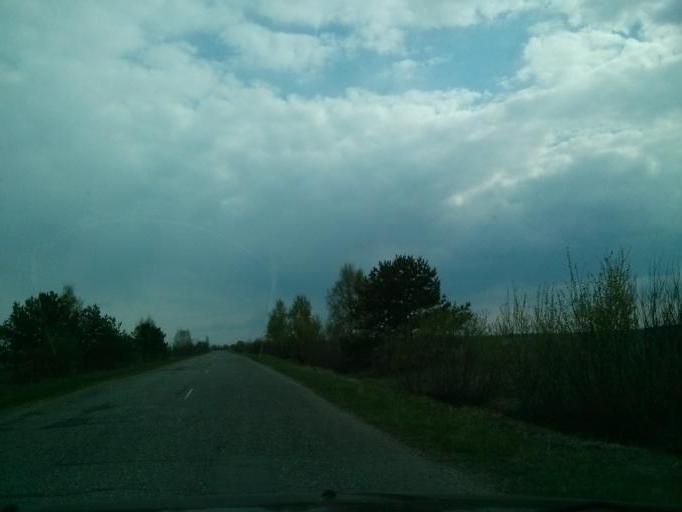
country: RU
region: Vladimir
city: Melenki
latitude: 55.3035
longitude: 41.7892
